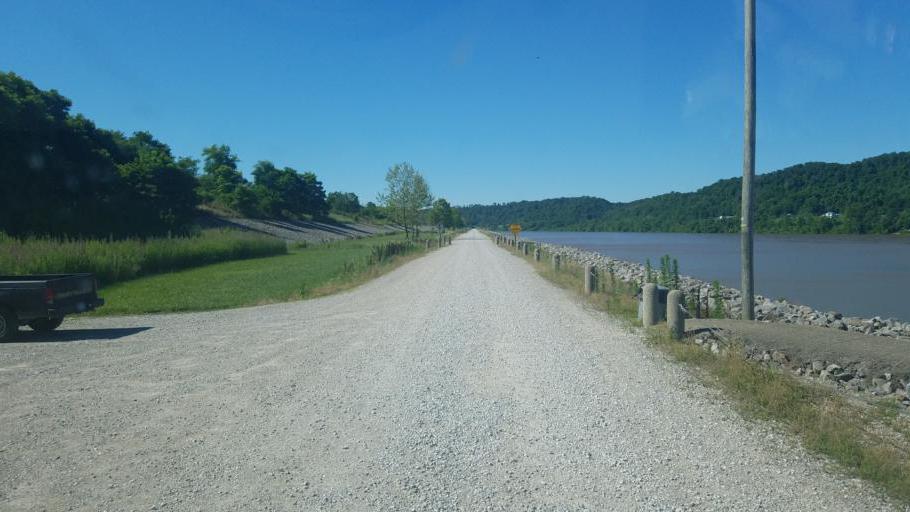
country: US
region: Ohio
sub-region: Gallia County
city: Gallipolis
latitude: 38.6799
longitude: -82.1829
